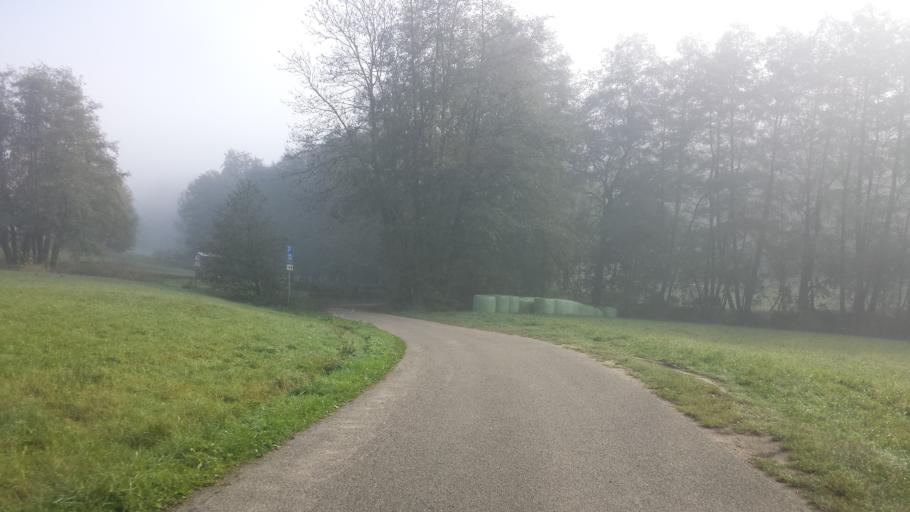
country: DE
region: Hesse
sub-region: Regierungsbezirk Darmstadt
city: Bensheim
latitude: 49.6893
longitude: 8.6893
